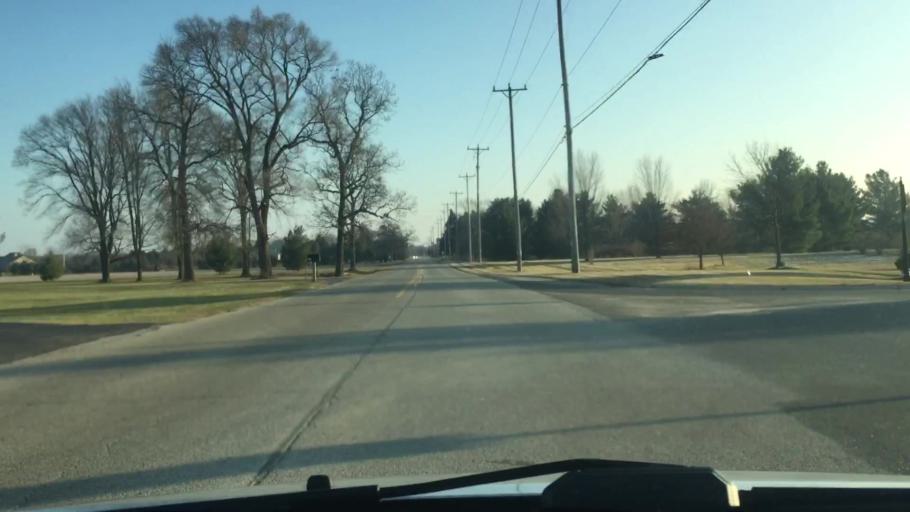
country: US
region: Wisconsin
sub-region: Waukesha County
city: Dousman
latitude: 43.0425
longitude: -88.4864
